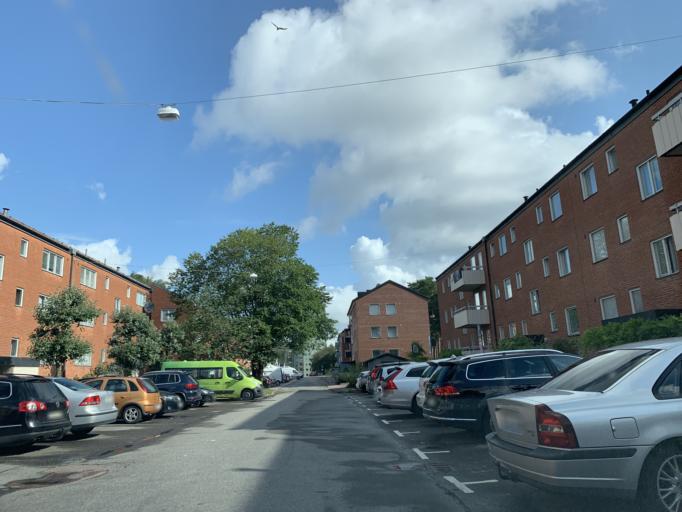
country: SE
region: Vaestra Goetaland
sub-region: Goteborg
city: Eriksbo
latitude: 57.7492
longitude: 12.0317
